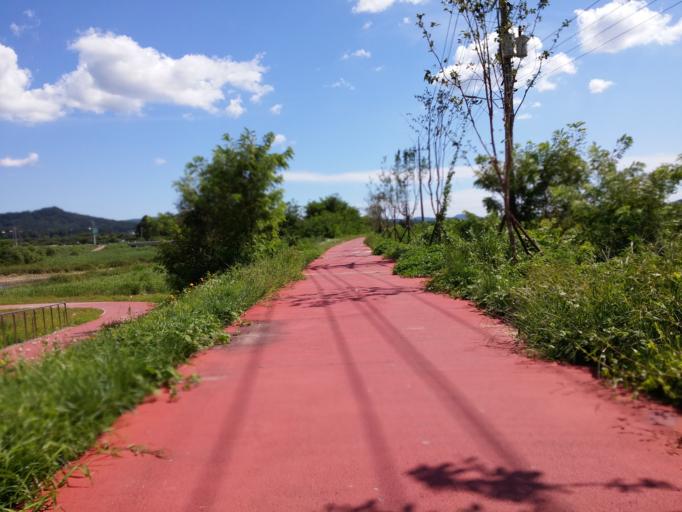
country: KR
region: Chungcheongbuk-do
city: Cheongju-si
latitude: 36.5872
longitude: 127.4998
